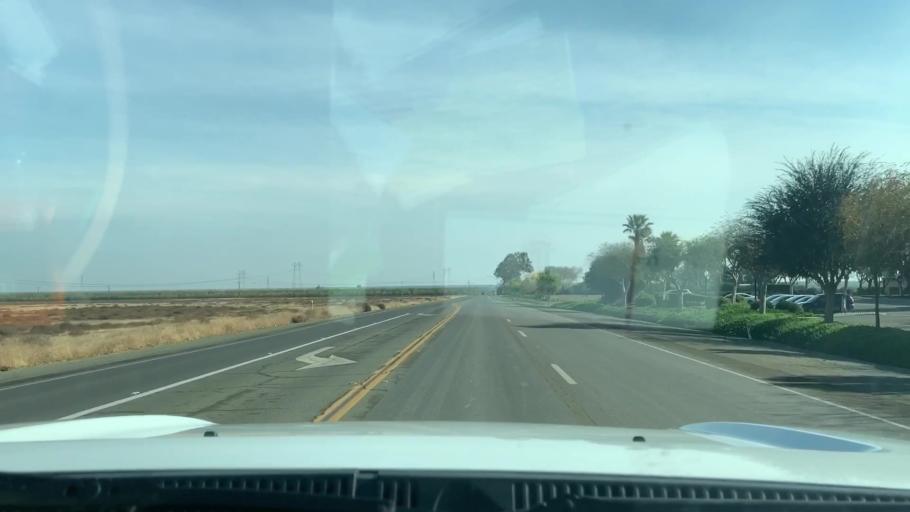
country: US
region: California
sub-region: Fresno County
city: Huron
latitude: 36.2545
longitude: -120.2356
